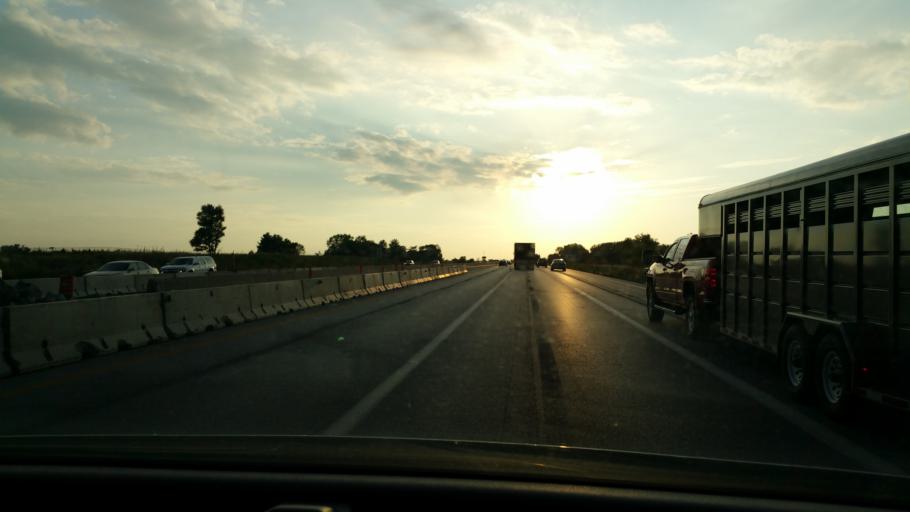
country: US
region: Iowa
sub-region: Polk County
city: Urbandale
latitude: 41.6517
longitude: -93.7558
